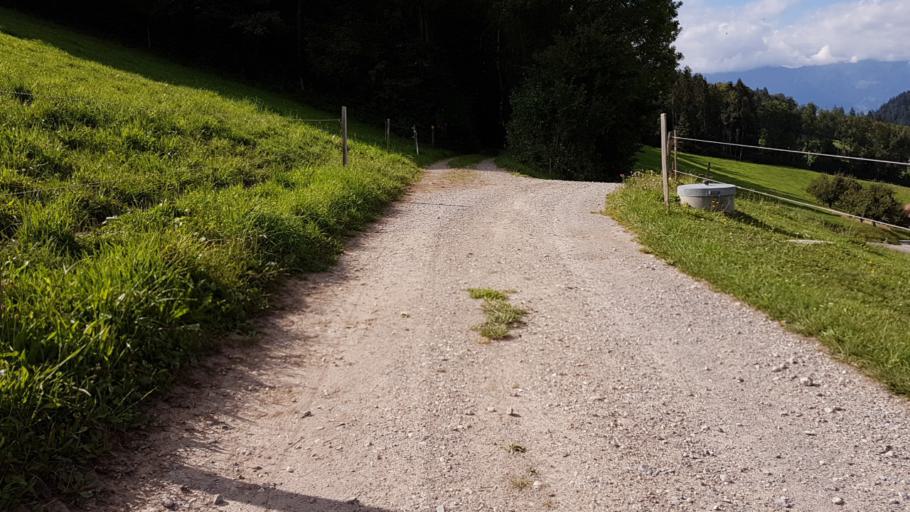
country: CH
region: Bern
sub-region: Bern-Mittelland District
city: Konolfingen
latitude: 46.8631
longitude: 7.6337
